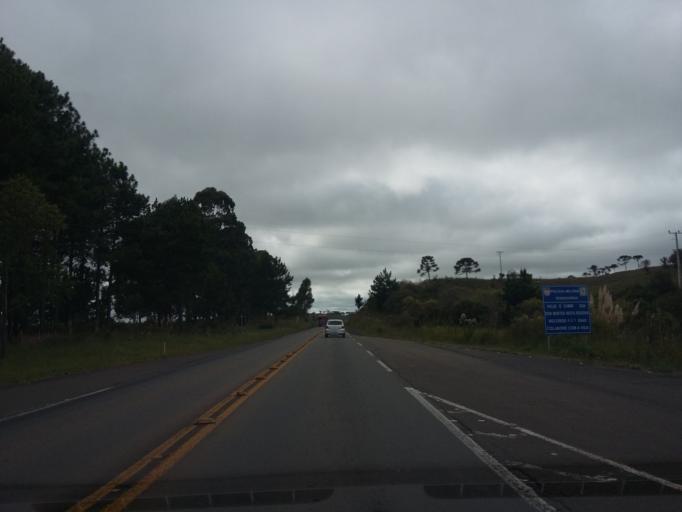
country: BR
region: Santa Catarina
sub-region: Lages
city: Lages
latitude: -27.8913
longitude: -50.1487
